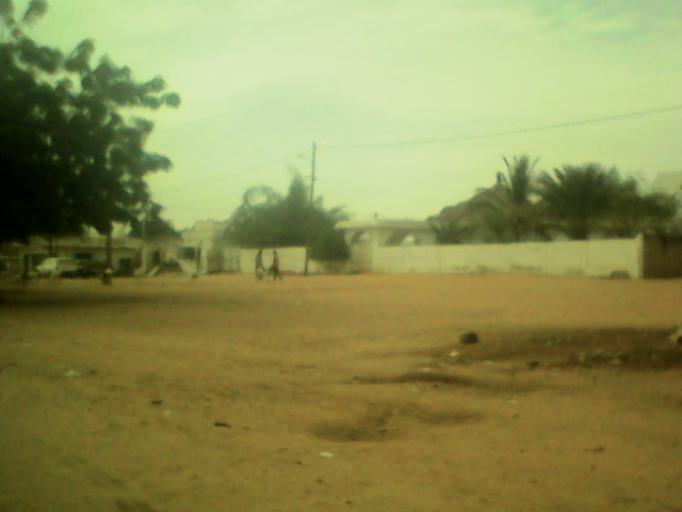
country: SN
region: Diourbel
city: Touba
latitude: 14.8831
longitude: -15.8840
